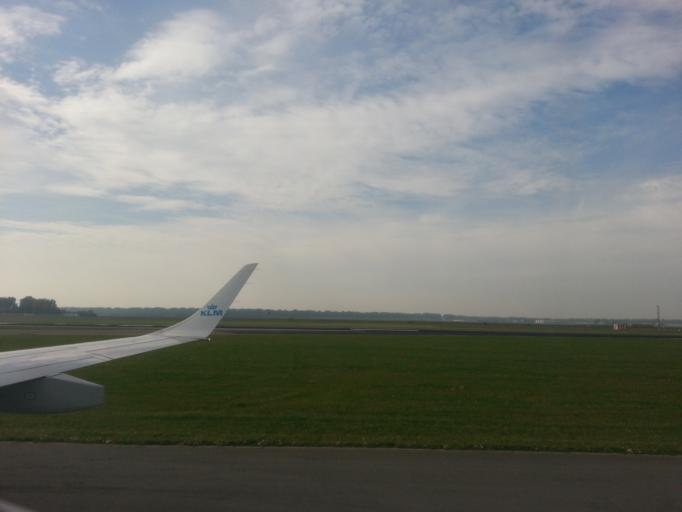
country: NL
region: North Holland
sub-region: Gemeente Aalsmeer
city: Aalsmeer
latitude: 52.3069
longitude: 4.7407
